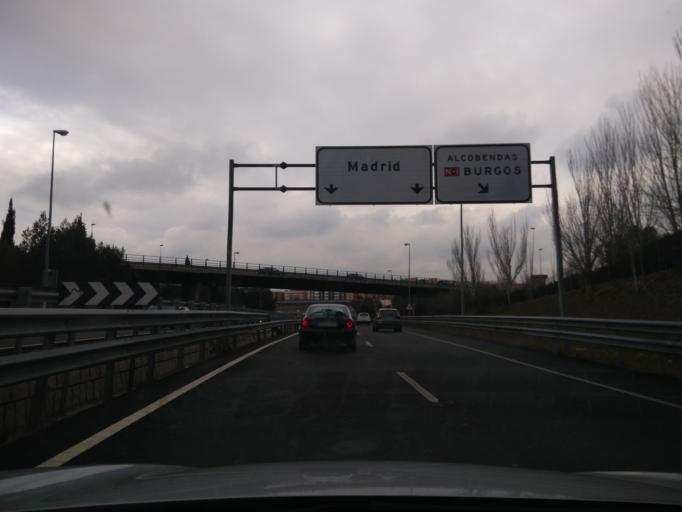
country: ES
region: Madrid
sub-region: Provincia de Madrid
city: Las Tablas
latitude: 40.5112
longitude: -3.6860
